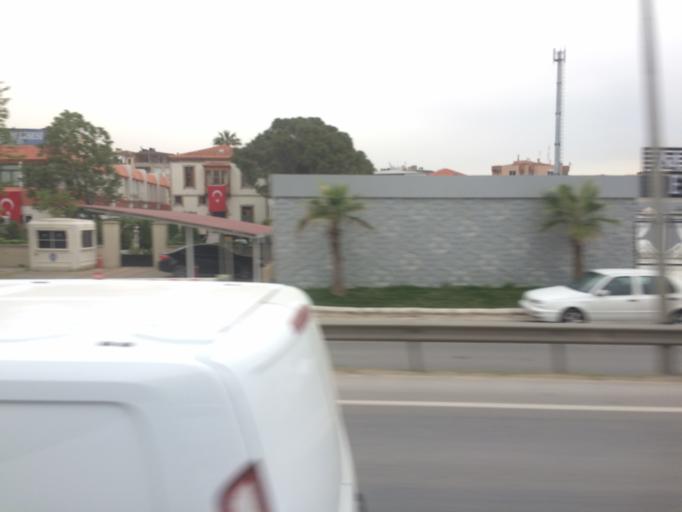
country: TR
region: Izmir
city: Karsiyaka
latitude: 38.4626
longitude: 27.1638
